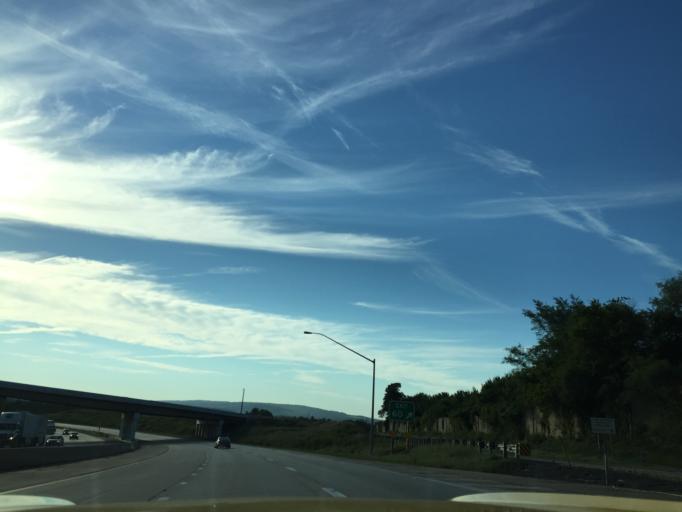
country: US
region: Pennsylvania
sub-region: Lehigh County
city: Fountain Hill
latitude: 40.5548
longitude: -75.4343
